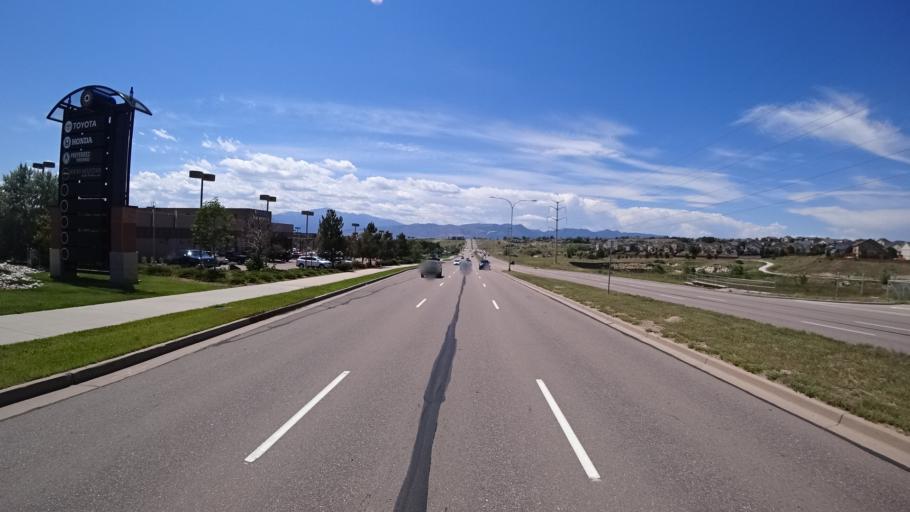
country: US
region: Colorado
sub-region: El Paso County
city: Black Forest
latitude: 38.9401
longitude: -104.7325
